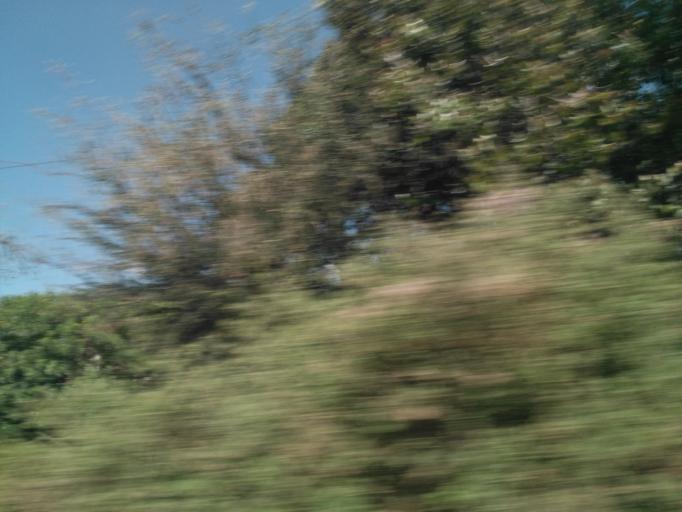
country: TZ
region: Dodoma
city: Dodoma
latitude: -6.1609
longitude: 35.7540
